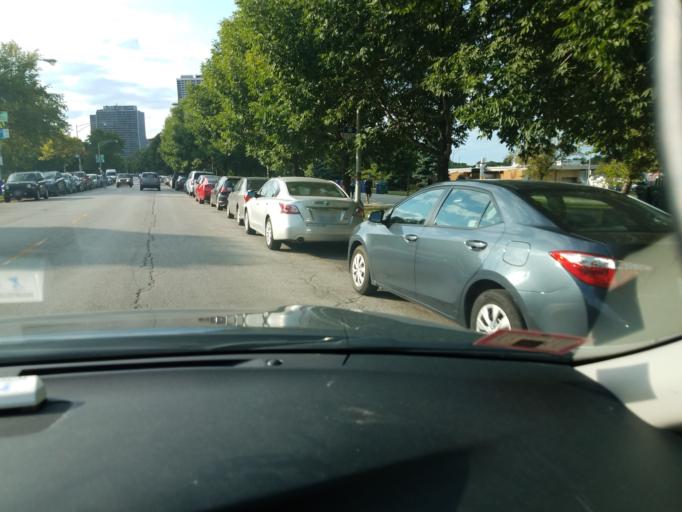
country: US
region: Illinois
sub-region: Cook County
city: Chicago
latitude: 41.9273
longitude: -87.6345
